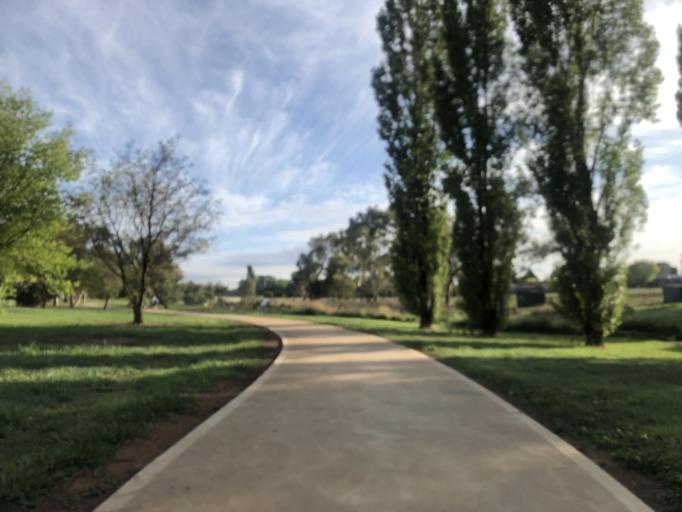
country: AU
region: New South Wales
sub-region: Orange Municipality
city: Orange
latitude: -33.2967
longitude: 149.0916
